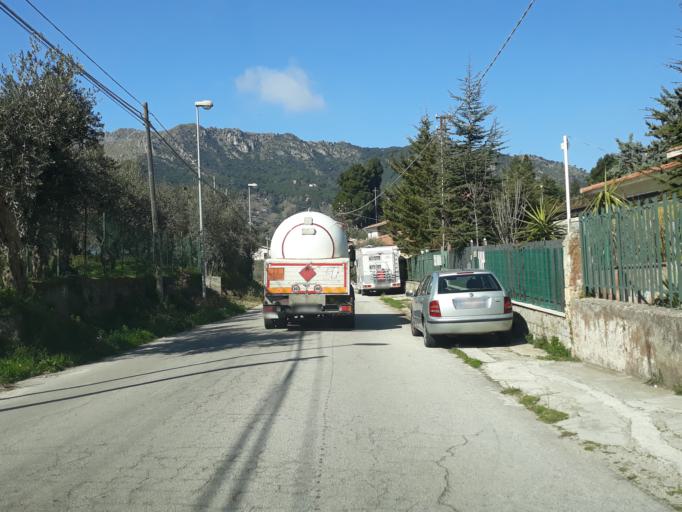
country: IT
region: Sicily
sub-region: Palermo
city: Piano dei Geli
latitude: 38.0852
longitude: 13.2638
